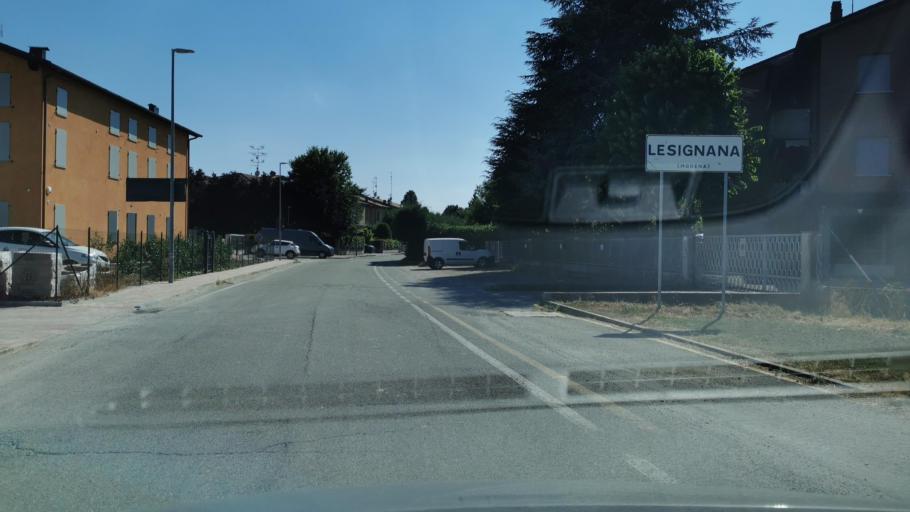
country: IT
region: Emilia-Romagna
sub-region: Provincia di Modena
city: Villanova
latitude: 44.6871
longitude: 10.8955
